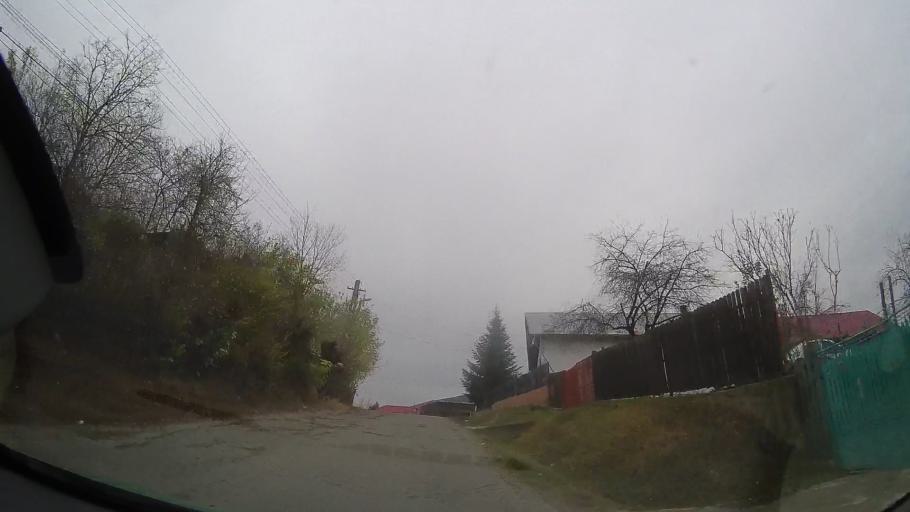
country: RO
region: Prahova
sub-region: Comuna Gornet-Cricov
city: Gornet-Cricov
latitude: 45.0556
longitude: 26.2923
